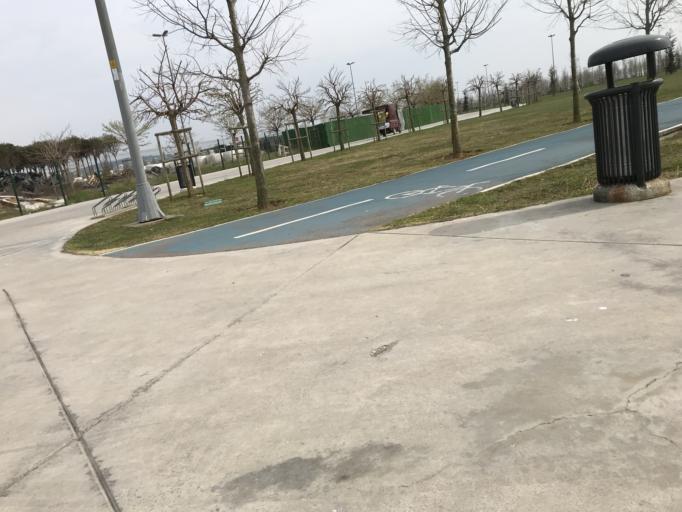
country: TR
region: Istanbul
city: Maltepe
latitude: 40.9319
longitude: 29.1146
